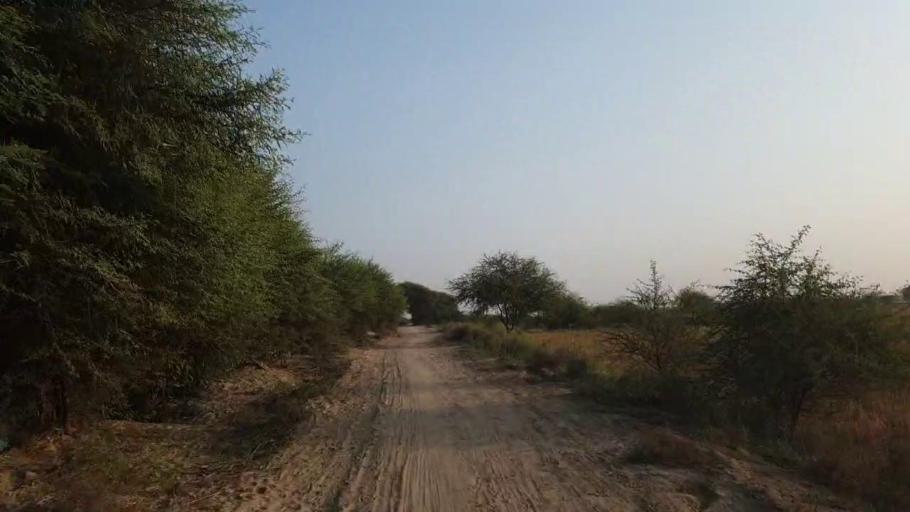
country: PK
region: Sindh
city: Kario
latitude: 24.8565
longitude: 68.6273
